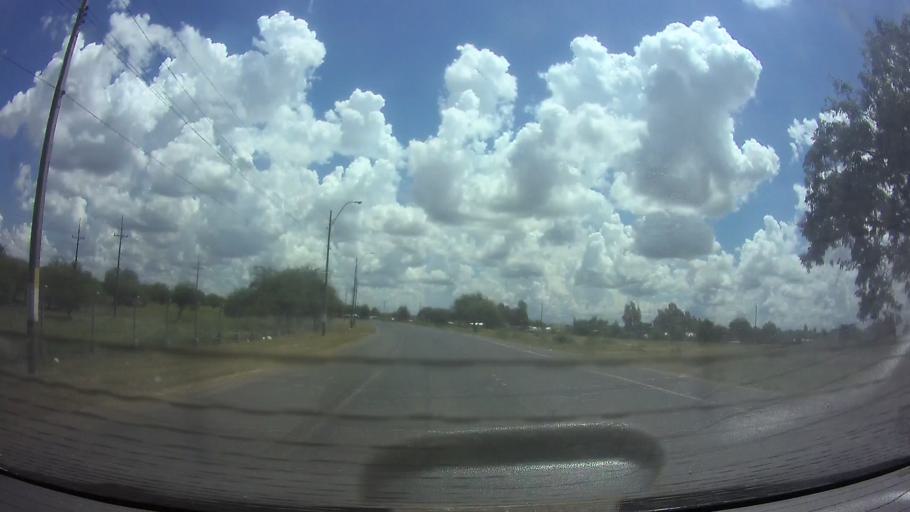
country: PY
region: Central
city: Colonia Mariano Roque Alonso
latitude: -25.1716
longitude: -57.5649
